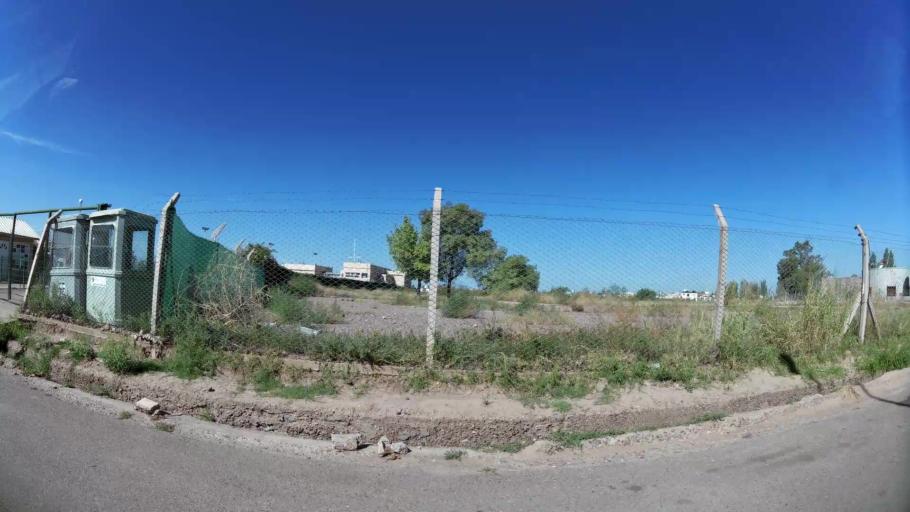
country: AR
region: Mendoza
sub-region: Departamento de Godoy Cruz
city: Godoy Cruz
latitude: -32.9503
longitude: -68.8134
